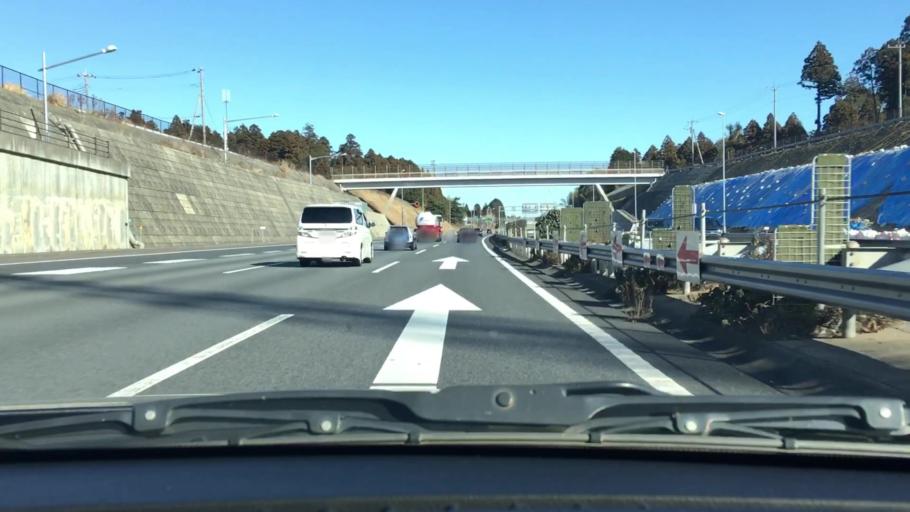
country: JP
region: Chiba
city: Shisui
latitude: 35.7277
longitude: 140.2935
